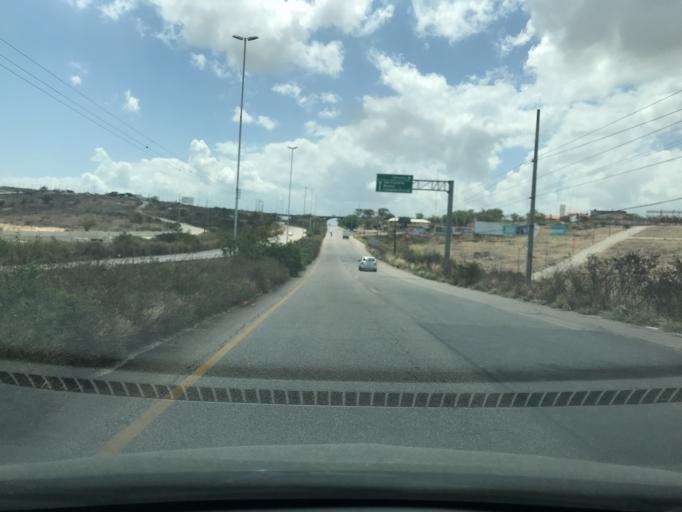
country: BR
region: Pernambuco
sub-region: Caruaru
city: Caruaru
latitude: -8.3070
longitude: -35.9596
